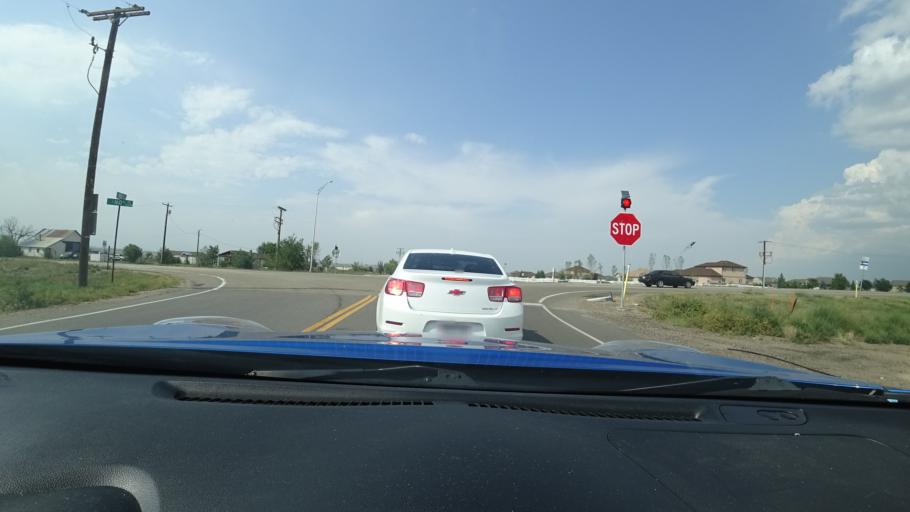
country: US
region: Colorado
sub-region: Adams County
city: Todd Creek
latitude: 39.9860
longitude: -104.9220
